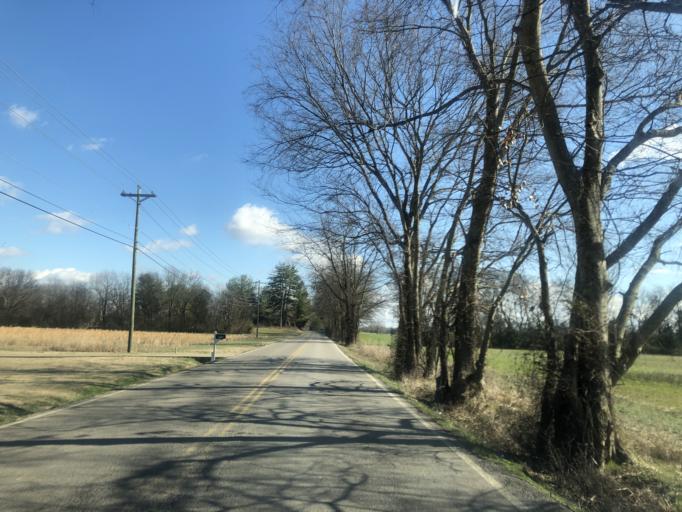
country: US
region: Tennessee
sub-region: Rutherford County
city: Smyrna
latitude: 35.8768
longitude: -86.5068
